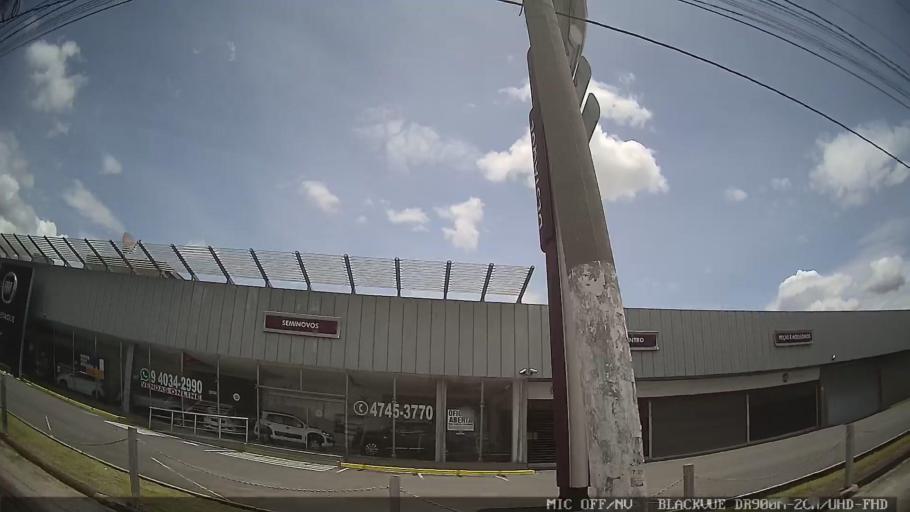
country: BR
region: Sao Paulo
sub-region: Suzano
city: Suzano
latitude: -23.5363
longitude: -46.3031
